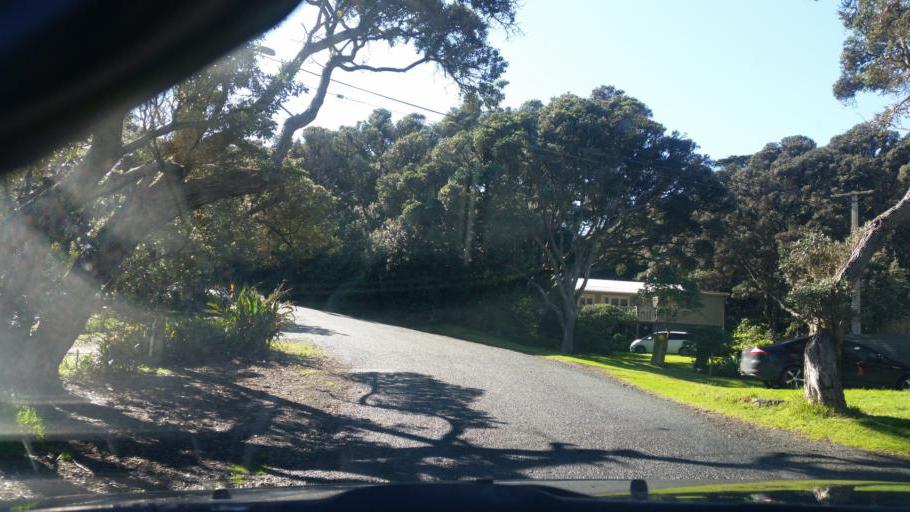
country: NZ
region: Northland
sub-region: Kaipara District
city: Dargaville
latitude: -35.9538
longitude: 173.7463
